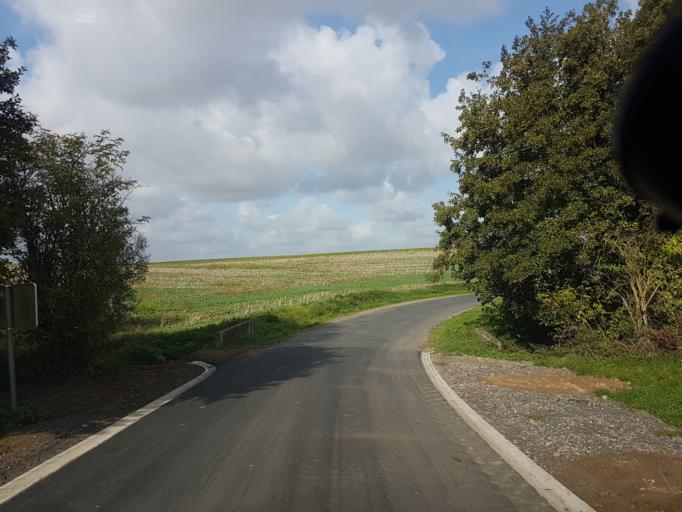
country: BE
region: Wallonia
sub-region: Province de Liege
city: Heron
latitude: 50.5642
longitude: 5.0865
